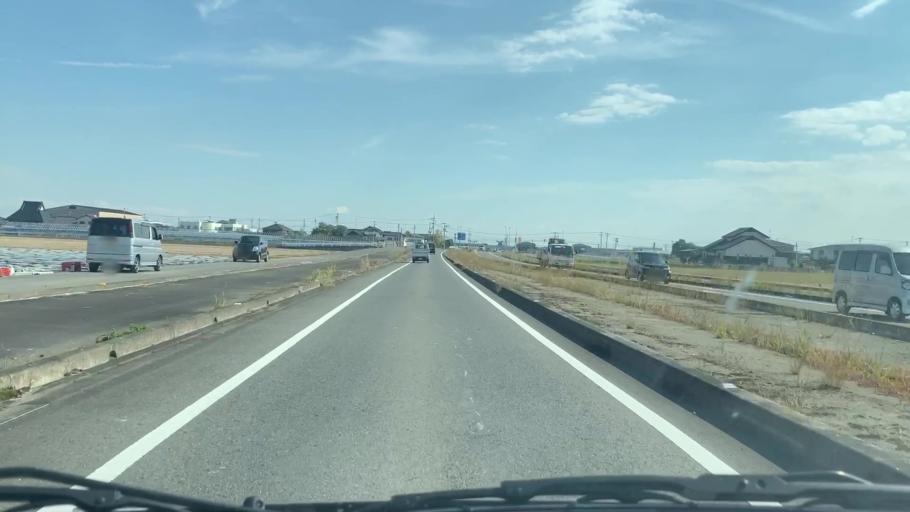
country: JP
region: Saga Prefecture
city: Saga-shi
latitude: 33.2214
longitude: 130.2048
